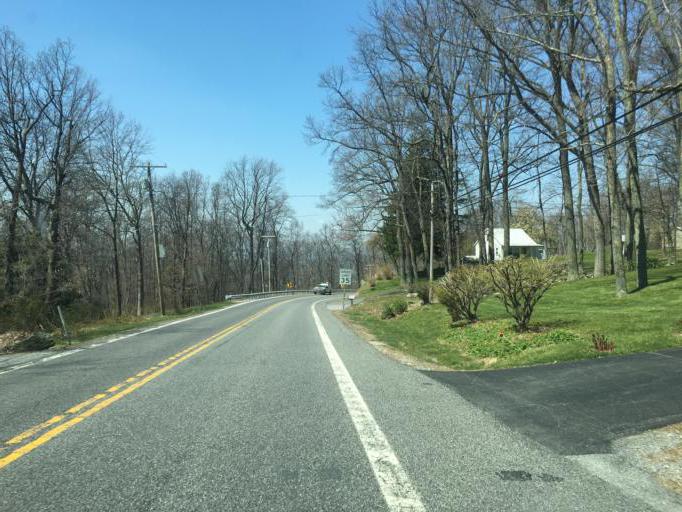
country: US
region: Maryland
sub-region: Washington County
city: Smithsburg
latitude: 39.6374
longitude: -77.5463
